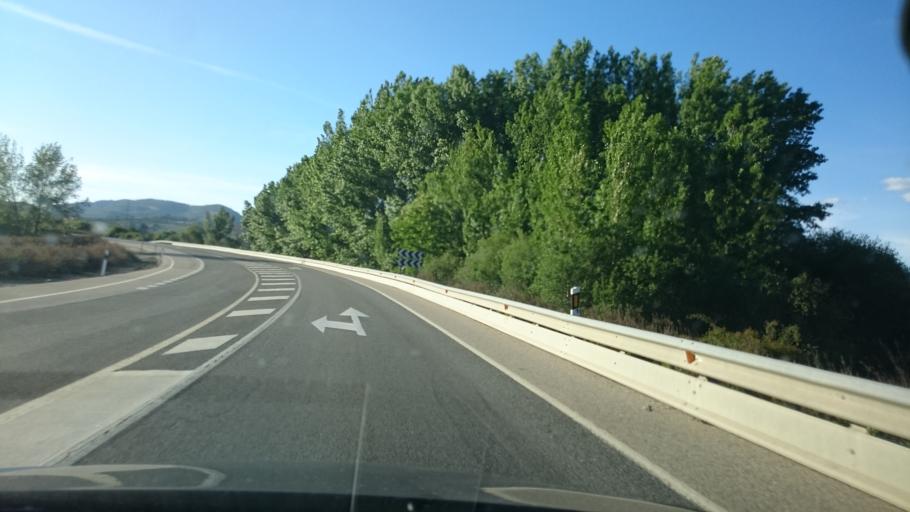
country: ES
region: Castille and Leon
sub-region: Provincia de Leon
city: Villadecanes
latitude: 42.5862
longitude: -6.7880
